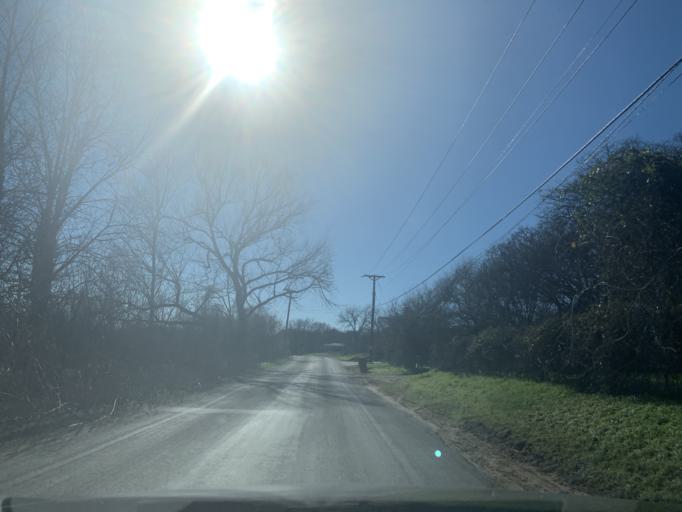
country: US
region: Texas
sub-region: Tarrant County
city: Haltom City
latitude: 32.7683
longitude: -97.2808
